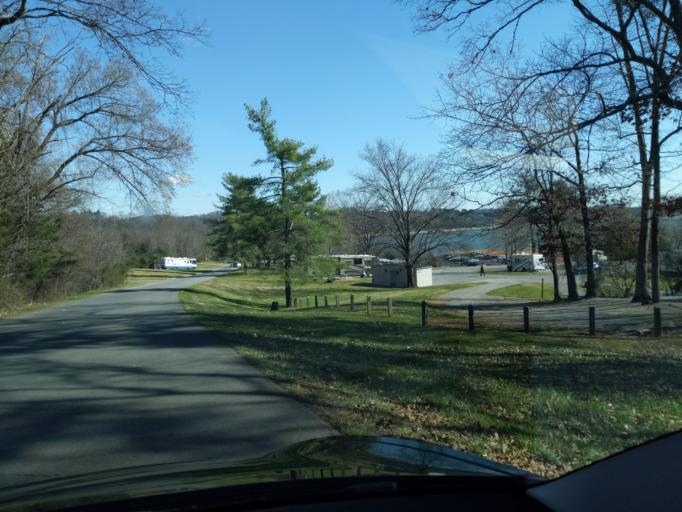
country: US
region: Tennessee
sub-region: Sevier County
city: Sevierville
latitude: 35.9560
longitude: -83.5372
